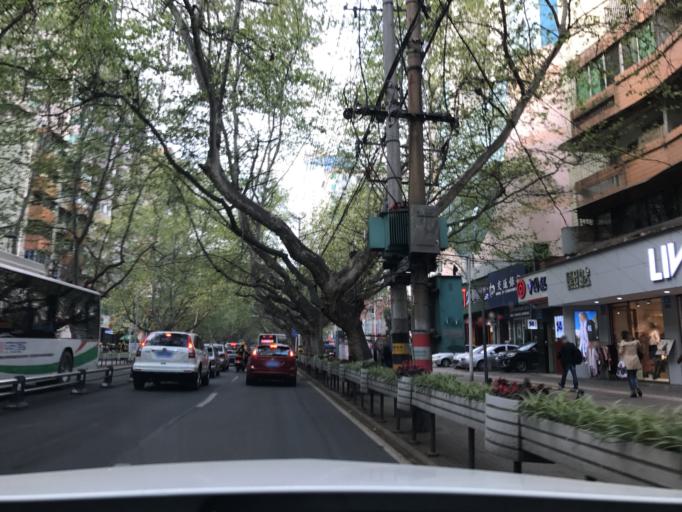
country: CN
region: Sichuan
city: Mianyang
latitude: 31.4582
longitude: 104.7480
